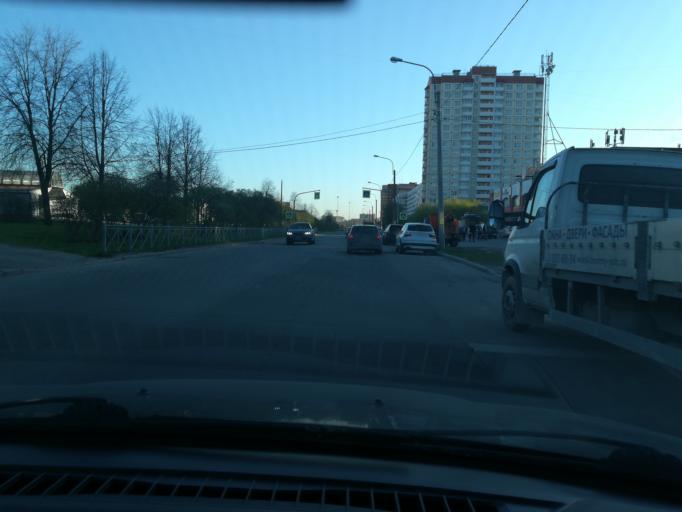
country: RU
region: St.-Petersburg
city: Dachnoye
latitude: 59.8555
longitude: 30.2423
